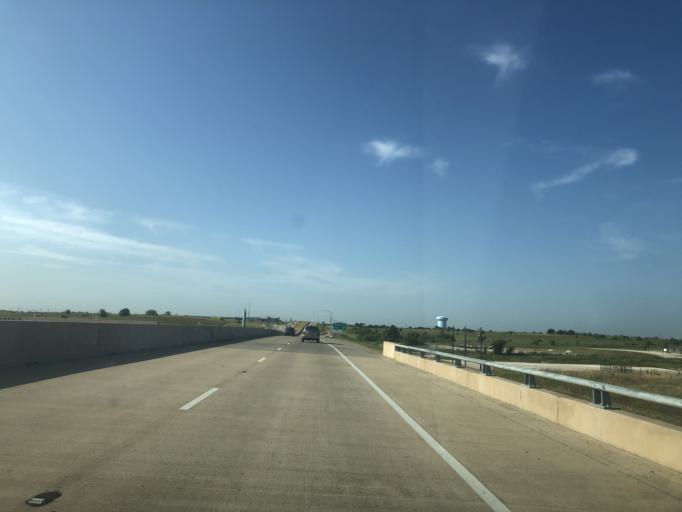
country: US
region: Texas
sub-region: Tarrant County
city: Crowley
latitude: 32.6155
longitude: -97.4127
